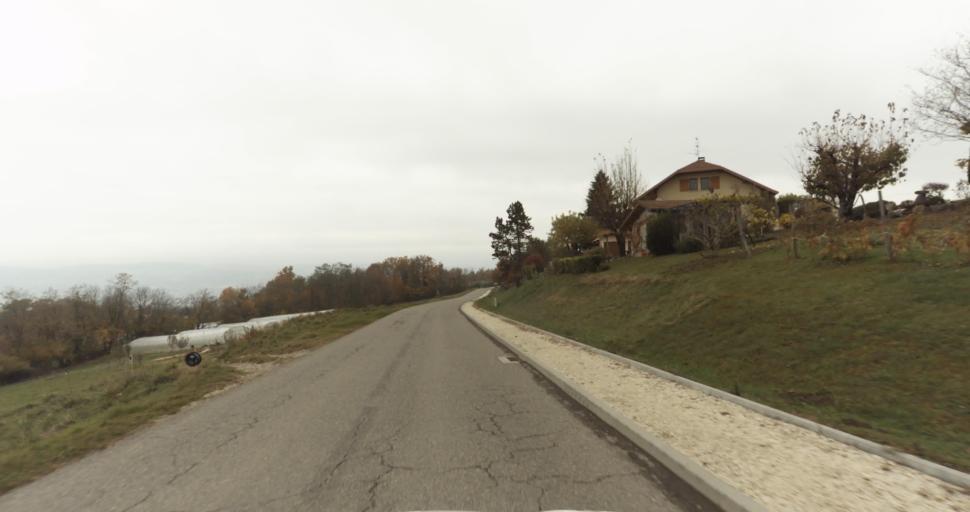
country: FR
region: Rhone-Alpes
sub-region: Departement de la Haute-Savoie
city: Saint-Felix
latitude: 45.7816
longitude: 5.9914
